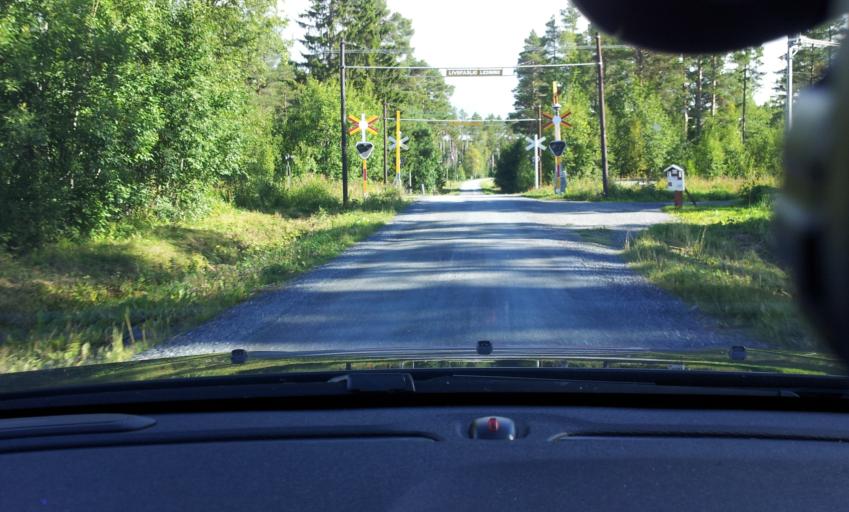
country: SE
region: Jaemtland
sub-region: Are Kommun
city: Jarpen
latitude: 63.2837
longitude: 13.7315
